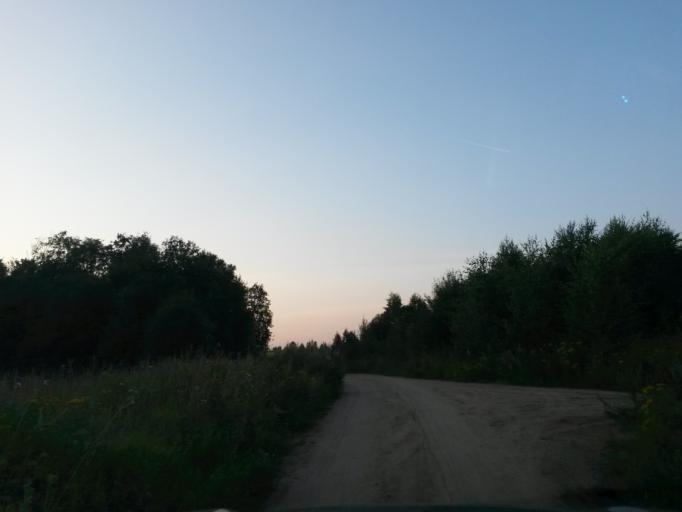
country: RU
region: Jaroslavl
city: Tutayev
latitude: 57.9374
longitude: 39.4446
